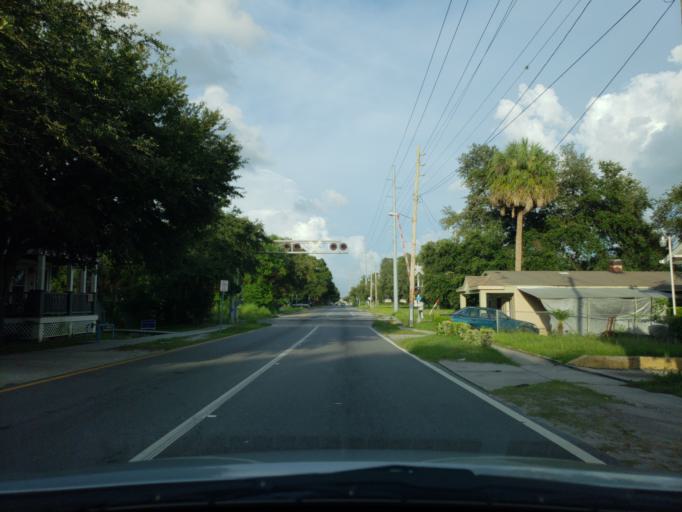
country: US
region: Florida
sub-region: Hillsborough County
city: Tampa
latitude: 27.9668
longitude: -82.4270
